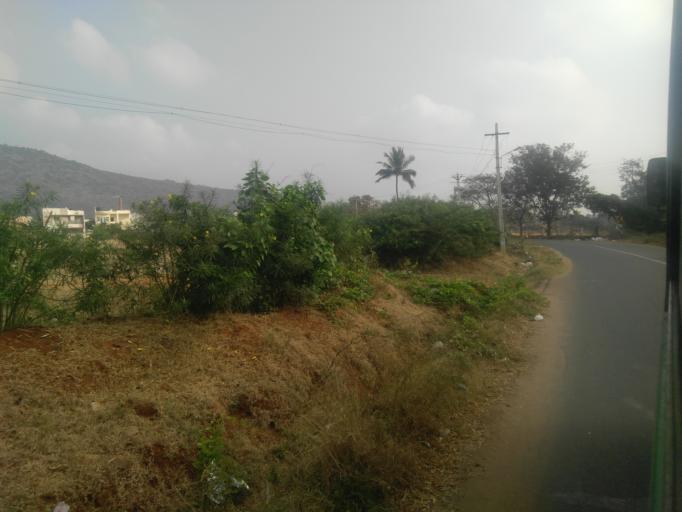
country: IN
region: Tamil Nadu
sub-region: Coimbatore
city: Perur
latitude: 11.0498
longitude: 76.8966
